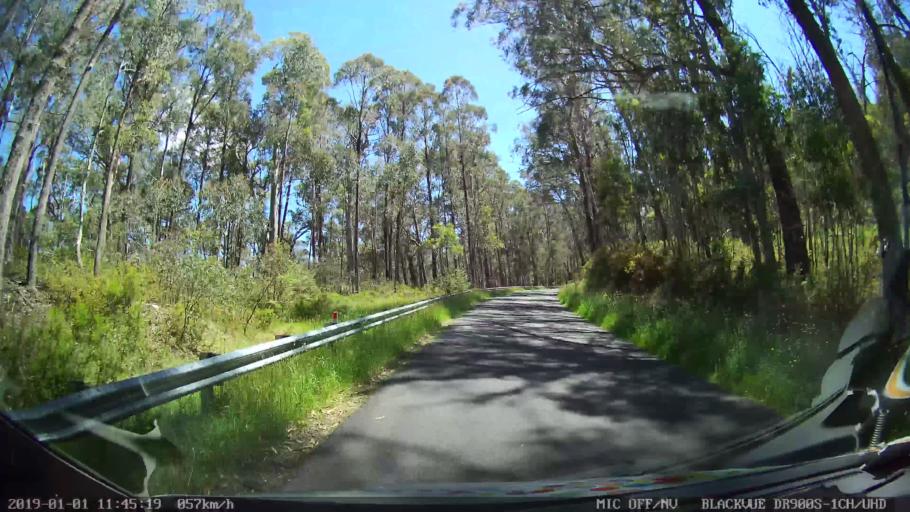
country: AU
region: New South Wales
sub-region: Snowy River
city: Jindabyne
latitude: -35.8976
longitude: 148.3953
